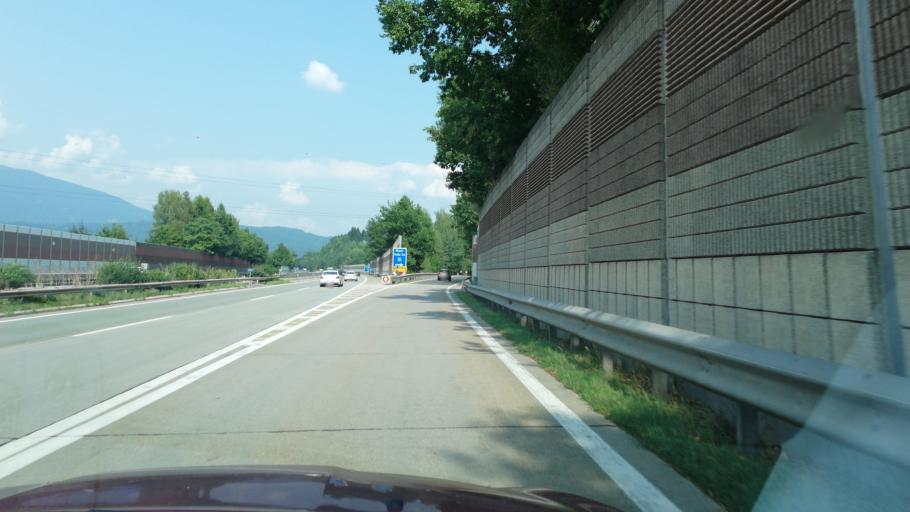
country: AT
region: Carinthia
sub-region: Villach Stadt
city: Villach
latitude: 46.5956
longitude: 13.8800
